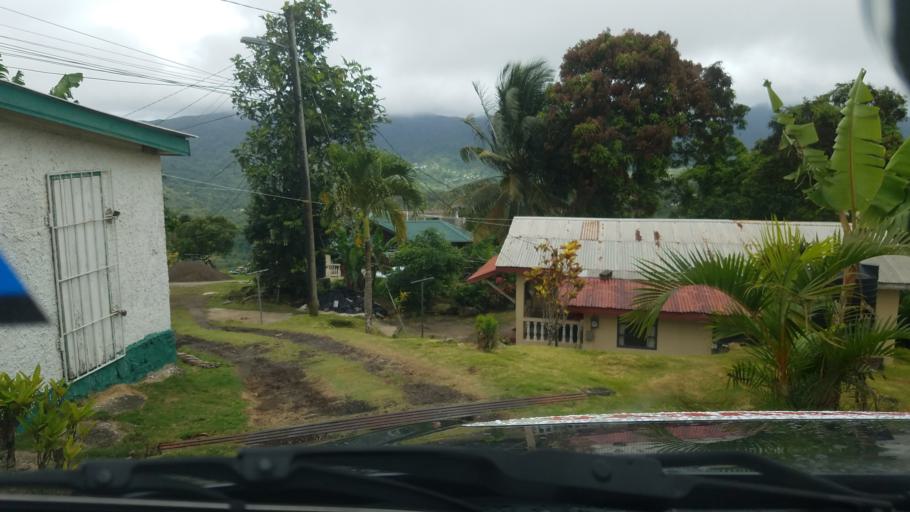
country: LC
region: Castries Quarter
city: Bisee
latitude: 14.0213
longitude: -60.9312
